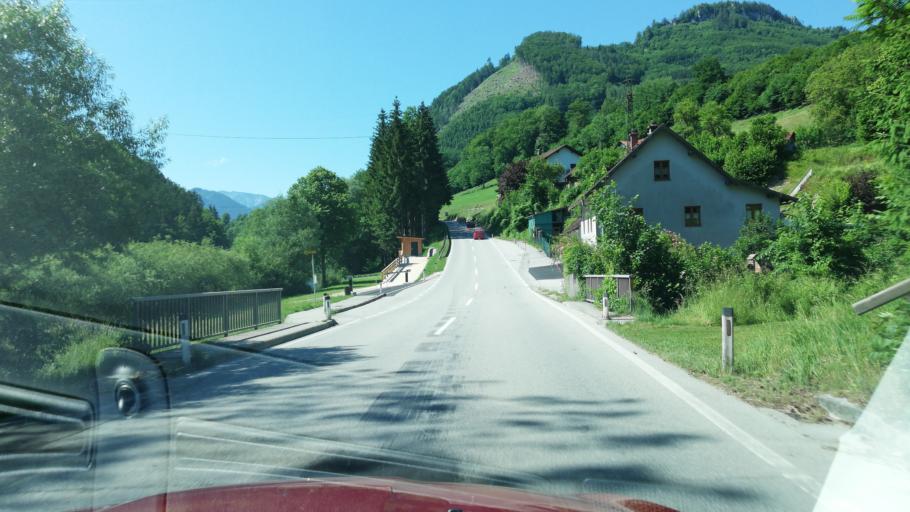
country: AT
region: Upper Austria
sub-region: Politischer Bezirk Kirchdorf an der Krems
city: Gruenburg
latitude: 47.9360
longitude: 14.2481
